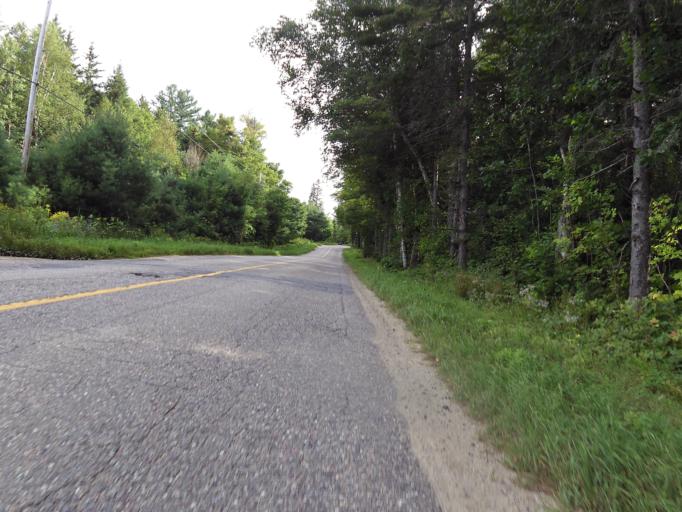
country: CA
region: Quebec
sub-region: Outaouais
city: Wakefield
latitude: 45.6734
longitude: -76.0097
